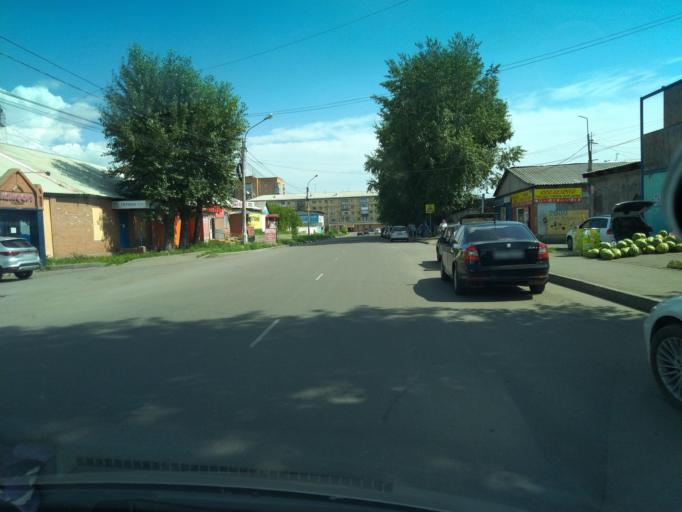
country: RU
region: Krasnoyarskiy
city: Krasnoyarsk
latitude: 56.0286
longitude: 92.8961
